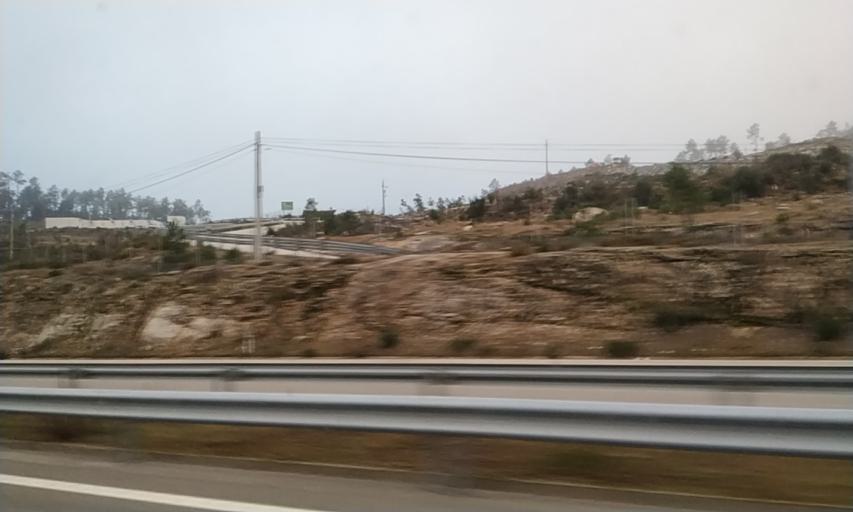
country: PT
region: Vila Real
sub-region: Ribeira de Pena
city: Ribeira de Pena
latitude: 41.5008
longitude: -7.7595
